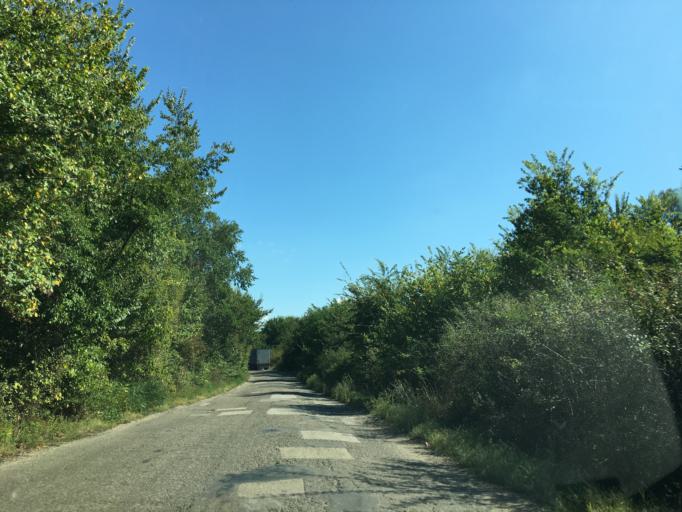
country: BG
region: Montana
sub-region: Obshtina Brusartsi
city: Brusartsi
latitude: 43.7694
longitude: 23.0694
